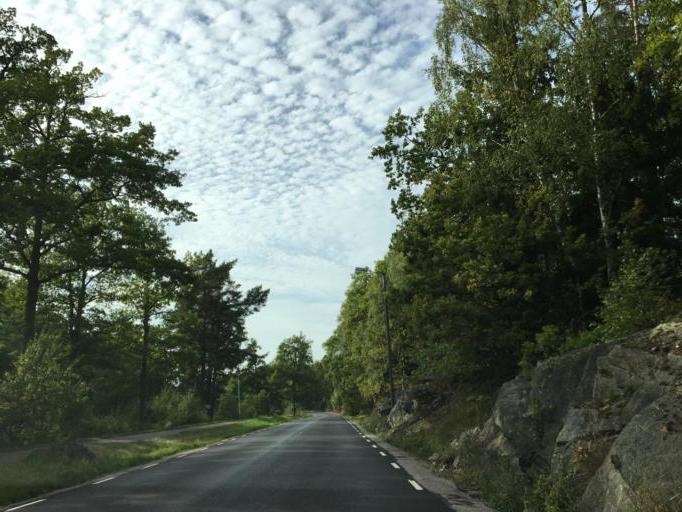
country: SE
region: Soedermanland
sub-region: Eskilstuna Kommun
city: Torshalla
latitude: 59.4488
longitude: 16.4448
